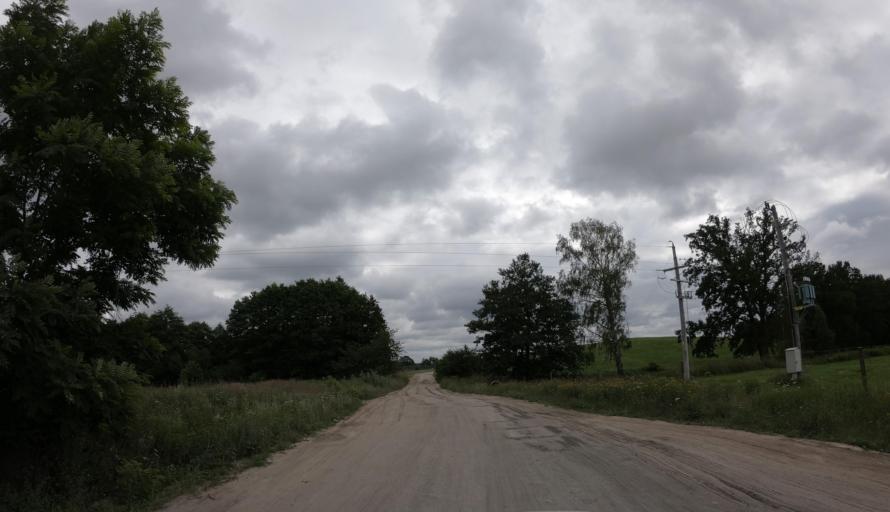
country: PL
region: West Pomeranian Voivodeship
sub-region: Powiat goleniowski
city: Przybiernow
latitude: 53.8241
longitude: 14.7501
